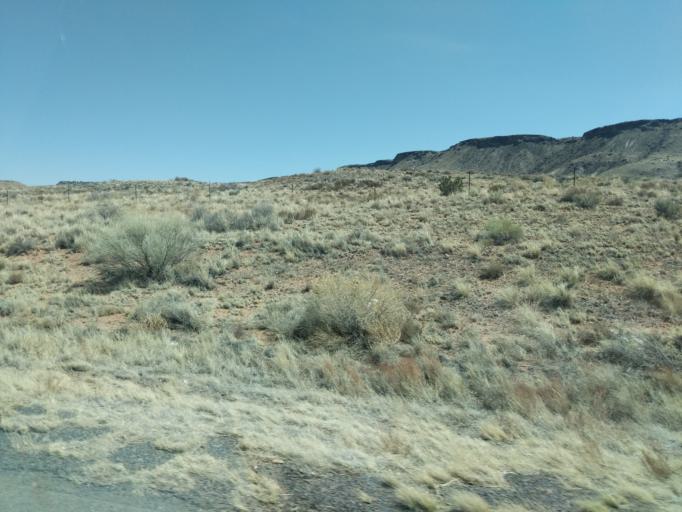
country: US
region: Arizona
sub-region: Navajo County
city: Dilkon
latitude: 35.4423
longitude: -110.0659
